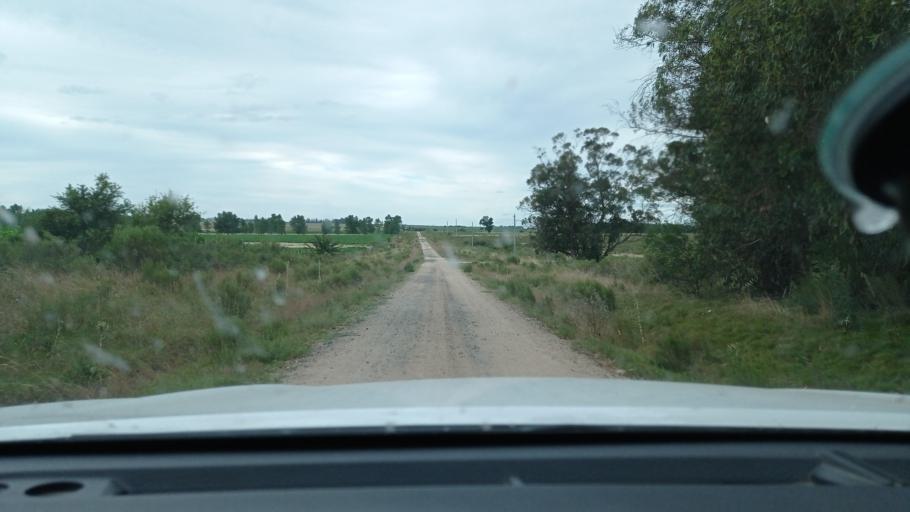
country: UY
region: Florida
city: Casupa
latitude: -34.1313
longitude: -55.7788
